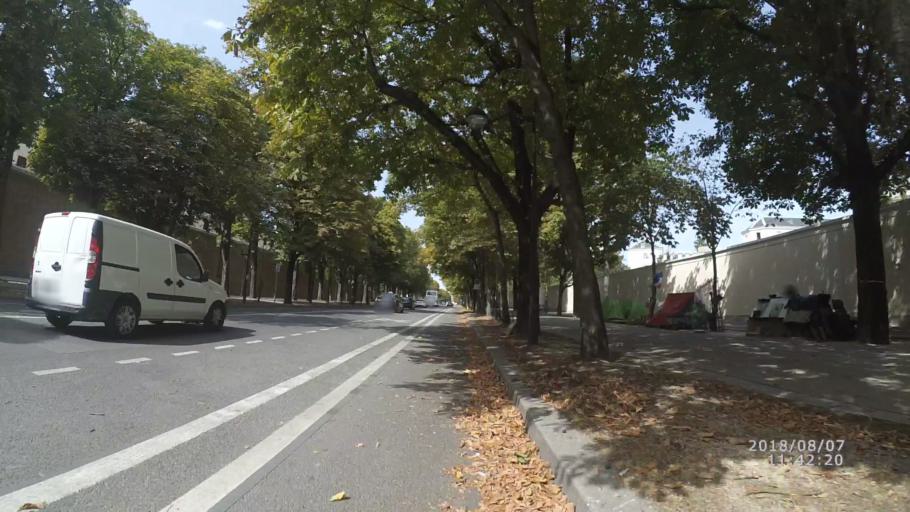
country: FR
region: Ile-de-France
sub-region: Paris
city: Paris
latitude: 48.8349
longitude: 2.3400
